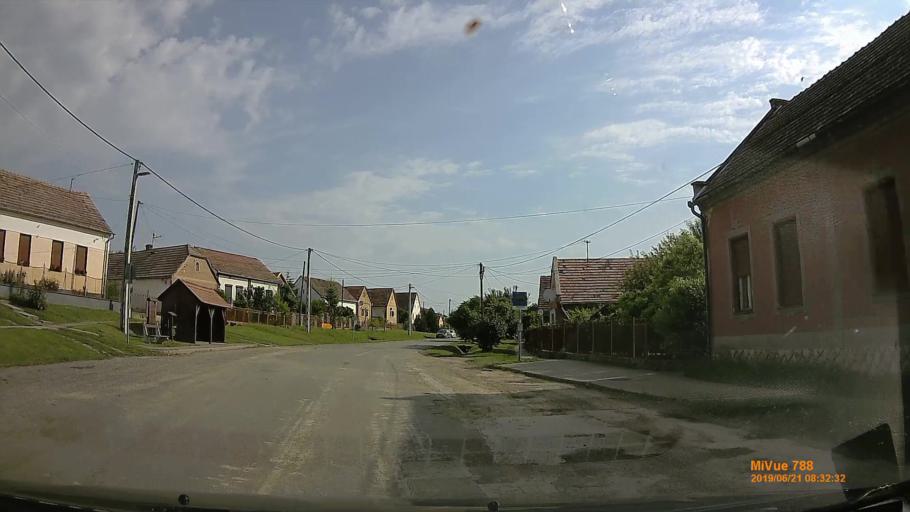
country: HU
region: Baranya
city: Buekkoesd
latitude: 46.1573
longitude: 17.8746
